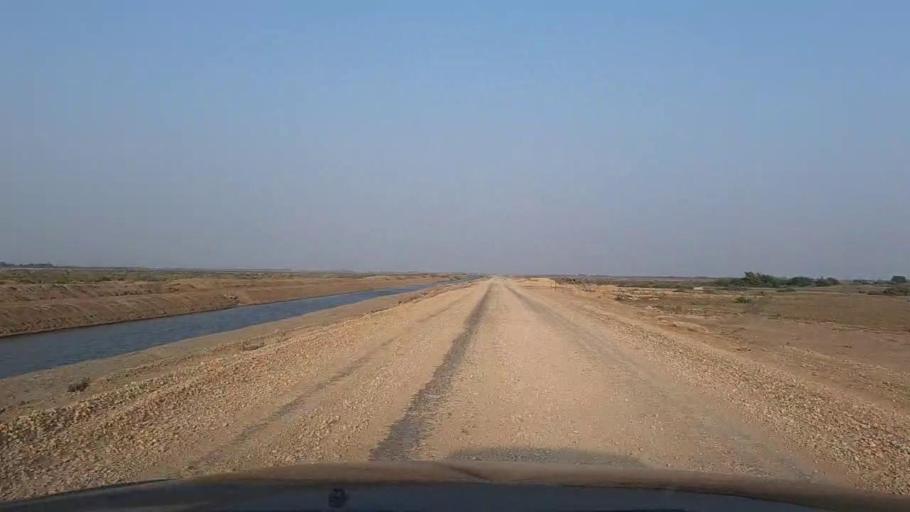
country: PK
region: Sindh
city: Mirpur Sakro
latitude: 24.4260
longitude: 67.7514
